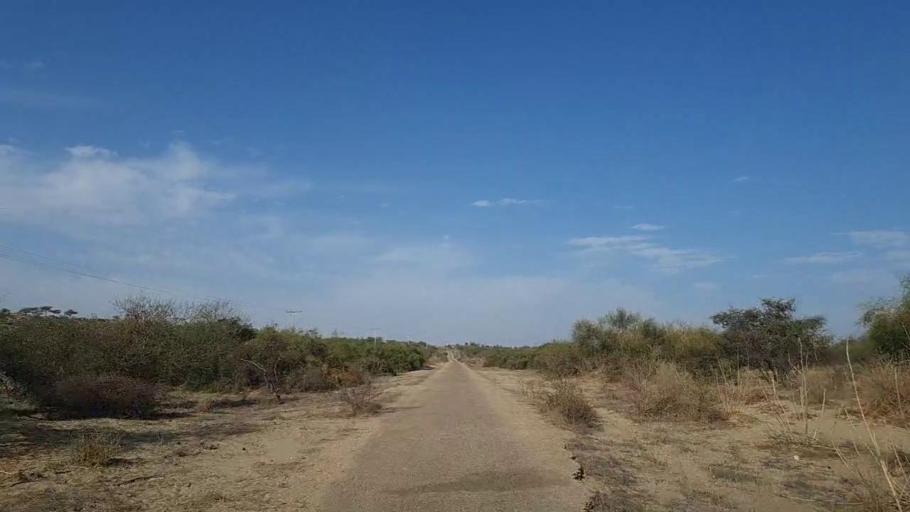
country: PK
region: Sindh
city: Naukot
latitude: 24.8519
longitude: 69.5204
